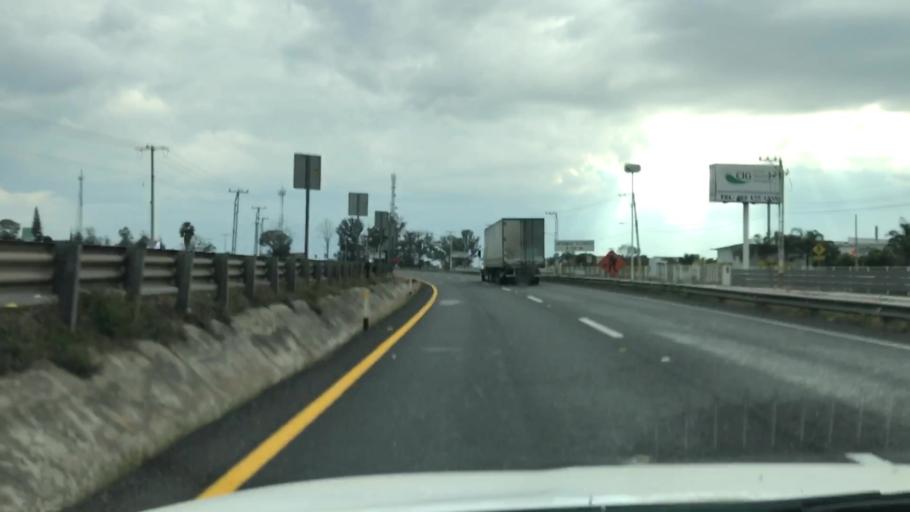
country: MX
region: Guanajuato
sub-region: Irapuato
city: San Ignacio de Rivera (Ojo de Agua)
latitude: 20.5680
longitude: -101.4459
